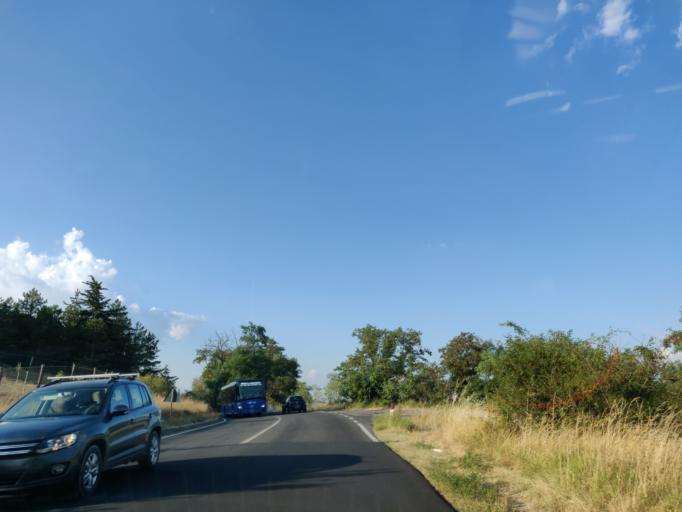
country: IT
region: Tuscany
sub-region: Provincia di Siena
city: Abbadia San Salvatore
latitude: 42.8705
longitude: 11.6845
